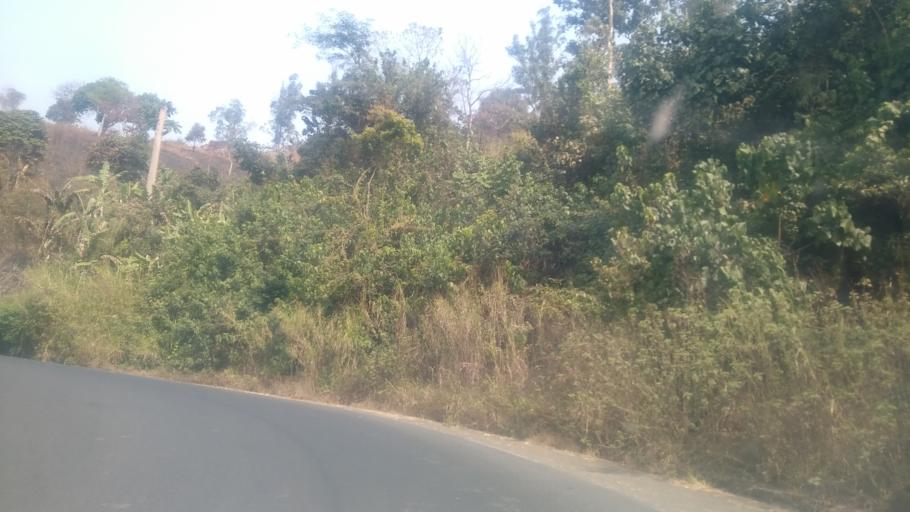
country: CM
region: West
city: Dschang
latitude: 5.4057
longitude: 10.0170
